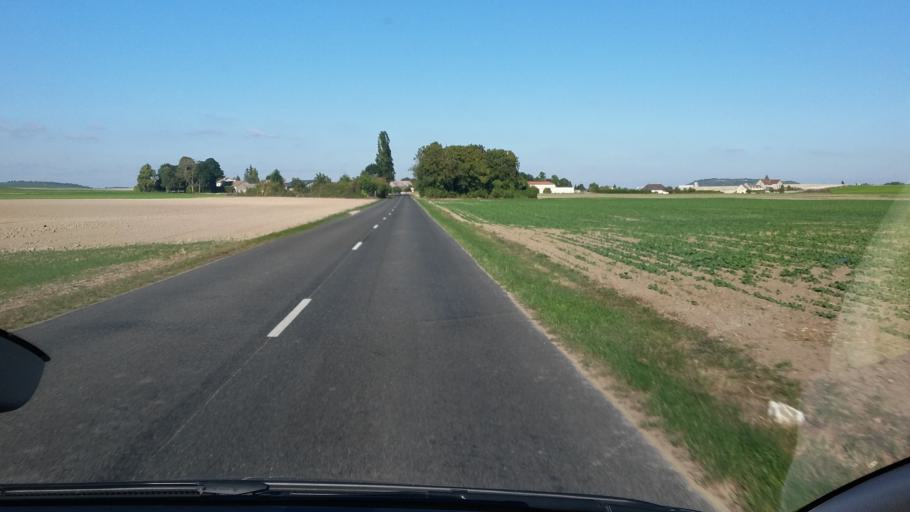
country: FR
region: Champagne-Ardenne
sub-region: Departement de la Marne
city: Fere-Champenoise
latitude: 48.8238
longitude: 3.9279
